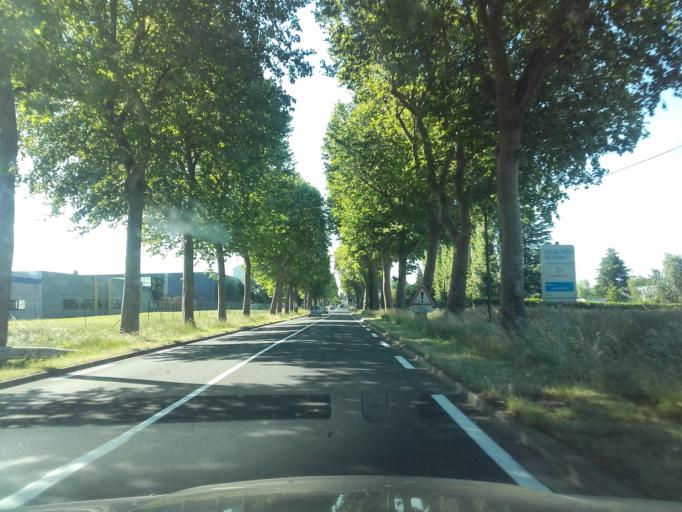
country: FR
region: Centre
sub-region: Departement d'Indre-et-Loire
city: Cormery
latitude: 47.2590
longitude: 0.8402
